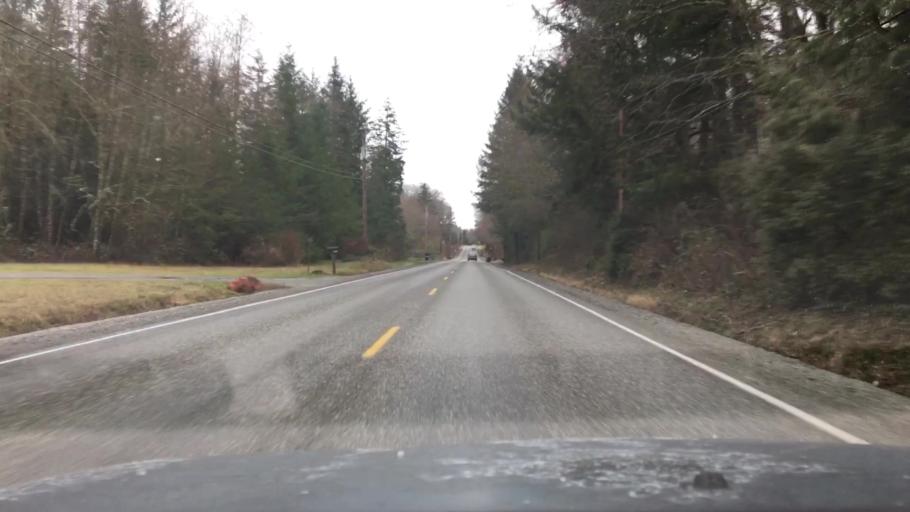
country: US
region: Washington
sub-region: Whatcom County
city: Sudden Valley
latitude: 48.6276
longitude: -122.3203
